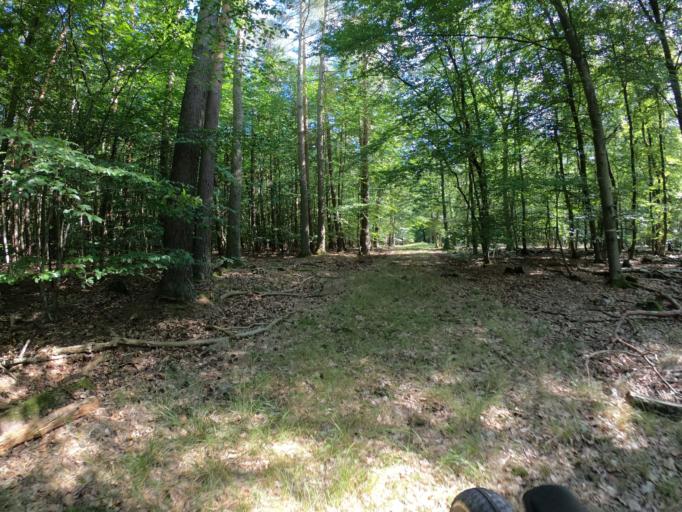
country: DE
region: Hesse
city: Langen
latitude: 50.0016
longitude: 8.6275
